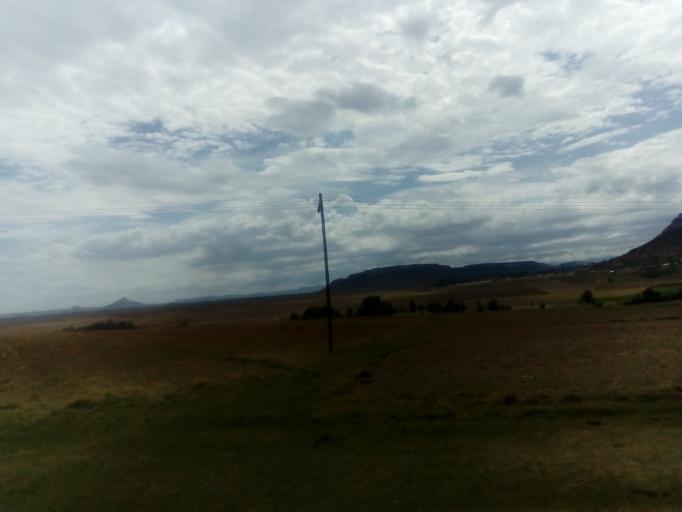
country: LS
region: Leribe
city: Leribe
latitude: -28.9881
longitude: 27.9863
